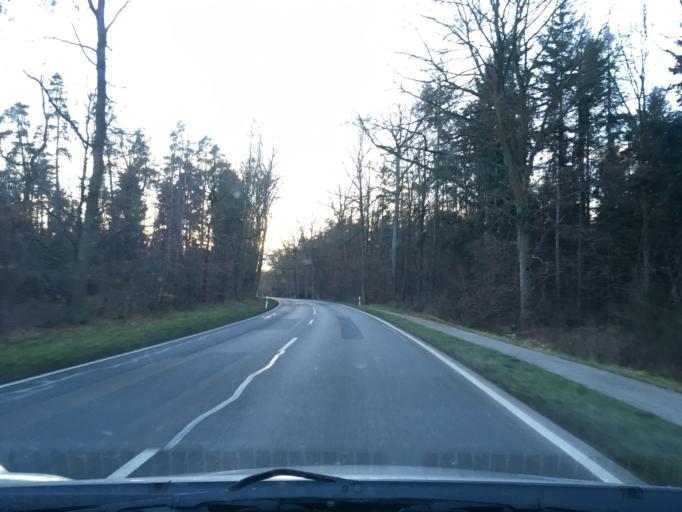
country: DE
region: Lower Saxony
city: Uelzen
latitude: 52.9786
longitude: 10.6100
